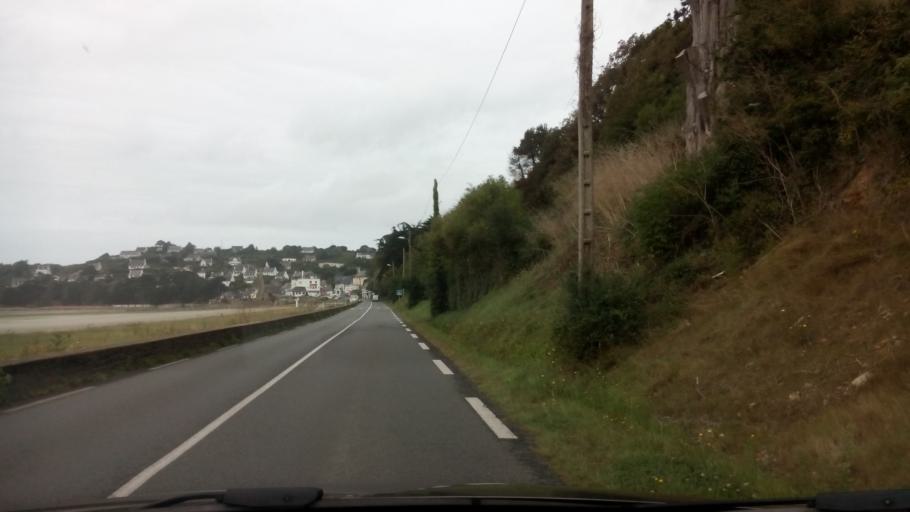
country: FR
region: Brittany
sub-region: Departement des Cotes-d'Armor
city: Locquemeau
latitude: 48.6800
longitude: -3.5690
